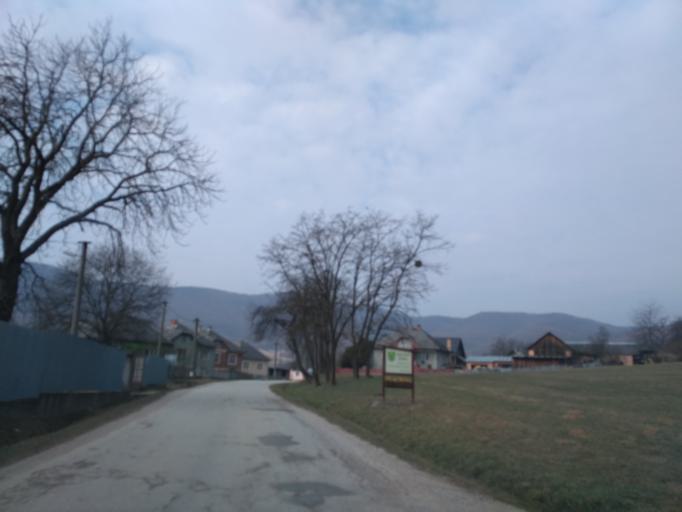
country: SK
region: Kosicky
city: Roznava
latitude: 48.6373
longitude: 20.4807
